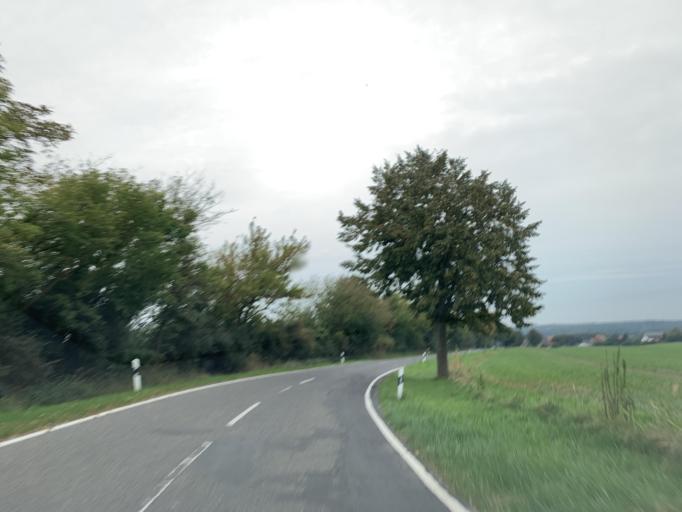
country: DE
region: Brandenburg
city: Mittenwalde
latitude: 53.3147
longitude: 13.6918
